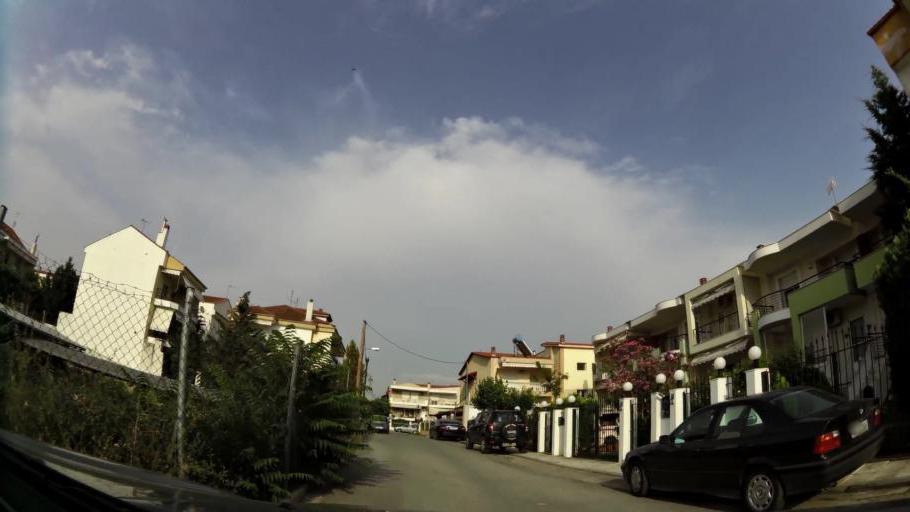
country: GR
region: Central Macedonia
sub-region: Nomos Thessalonikis
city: Oraiokastro
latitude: 40.7195
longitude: 22.9096
